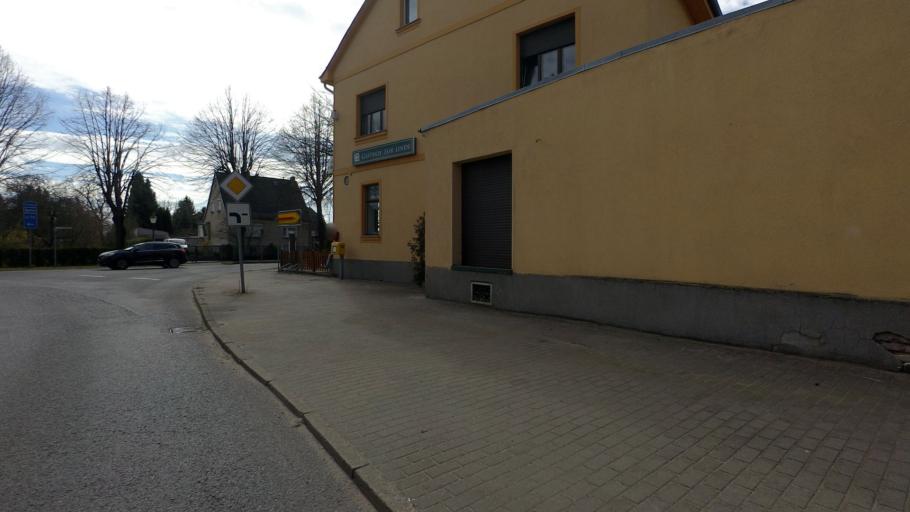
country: DE
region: Berlin
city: Buchholz
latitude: 52.6539
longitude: 13.4346
